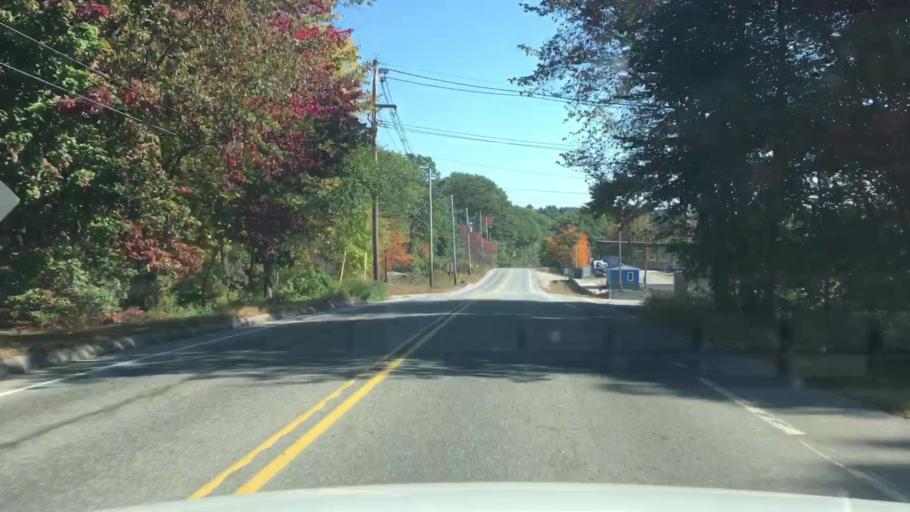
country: US
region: Maine
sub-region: Androscoggin County
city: Lisbon Falls
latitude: 43.9941
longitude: -70.0557
